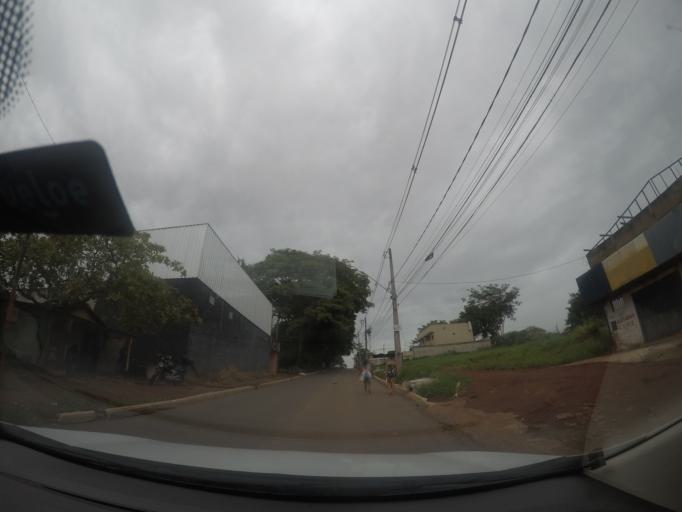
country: BR
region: Goias
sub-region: Goiania
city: Goiania
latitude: -16.6312
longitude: -49.3070
